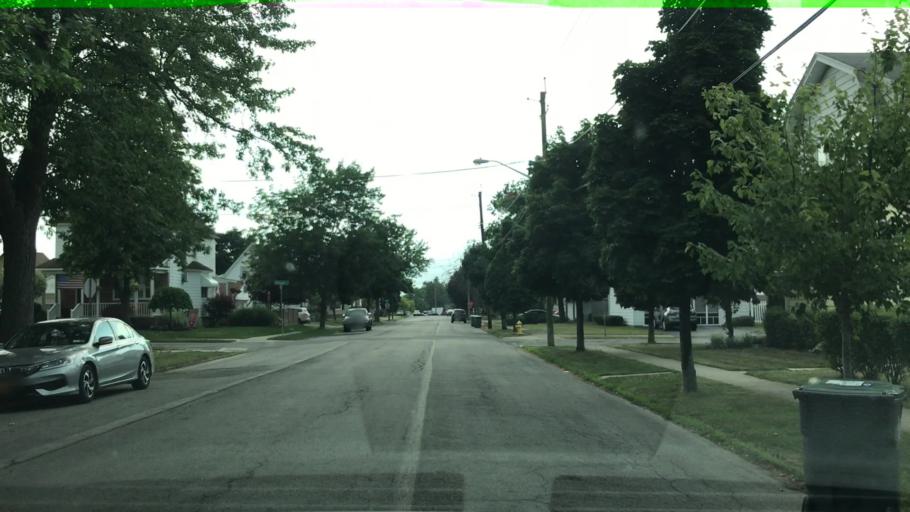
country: US
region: New York
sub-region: Erie County
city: Depew
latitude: 42.9139
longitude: -78.6932
